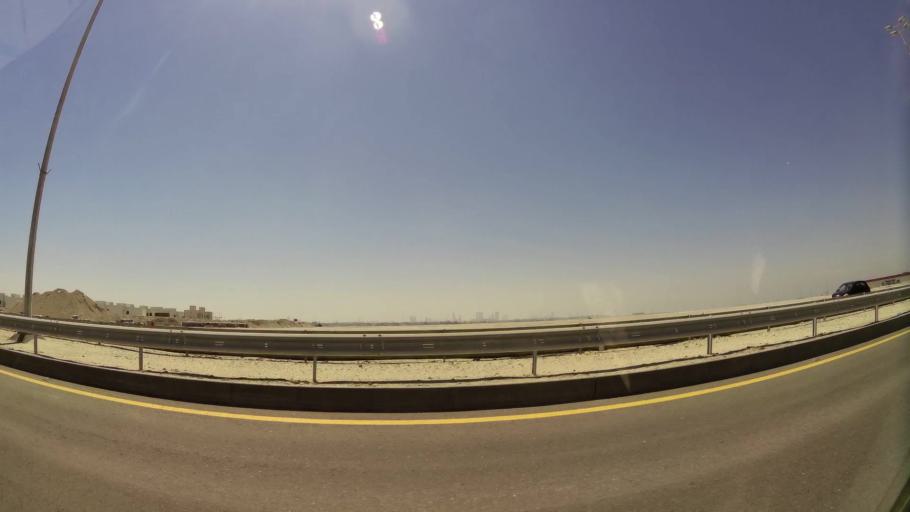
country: BH
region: Muharraq
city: Al Muharraq
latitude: 26.3041
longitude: 50.6318
